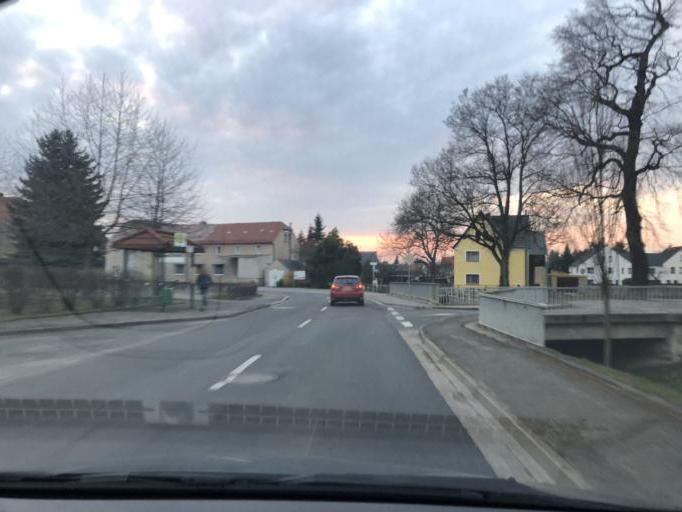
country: DE
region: Saxony
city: Haselbachtal
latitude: 51.2389
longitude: 14.0384
